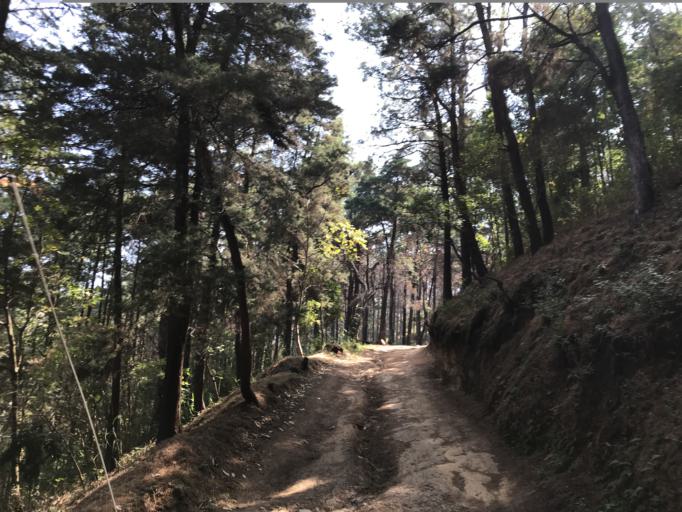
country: GT
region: Guatemala
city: Petapa
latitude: 14.4837
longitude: -90.5547
